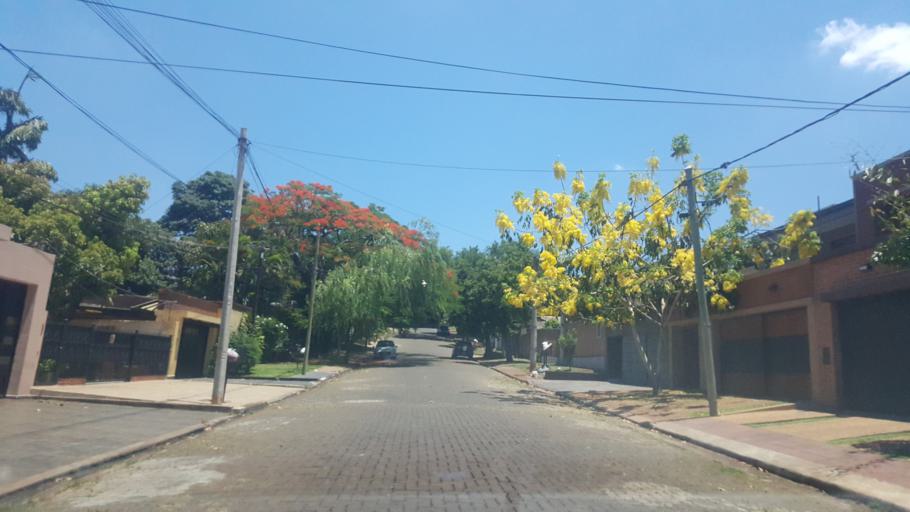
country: AR
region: Misiones
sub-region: Departamento de Capital
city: Posadas
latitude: -27.3619
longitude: -55.9057
